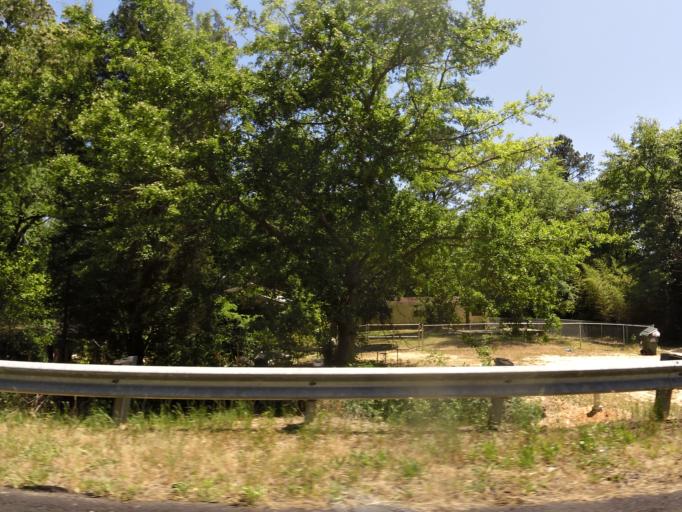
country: US
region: South Carolina
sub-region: Aiken County
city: Warrenville
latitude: 33.5570
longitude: -81.7992
